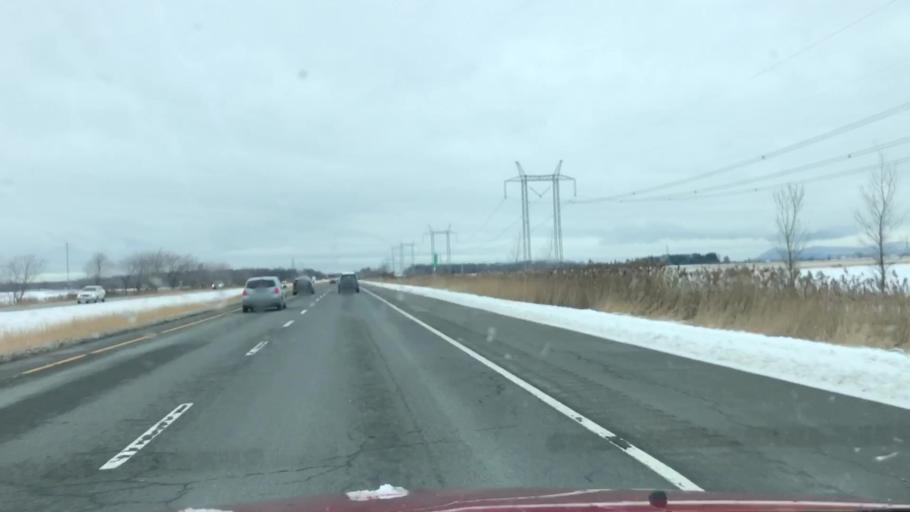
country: CA
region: Quebec
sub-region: Monteregie
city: Rougemont
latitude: 45.3811
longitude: -73.0625
